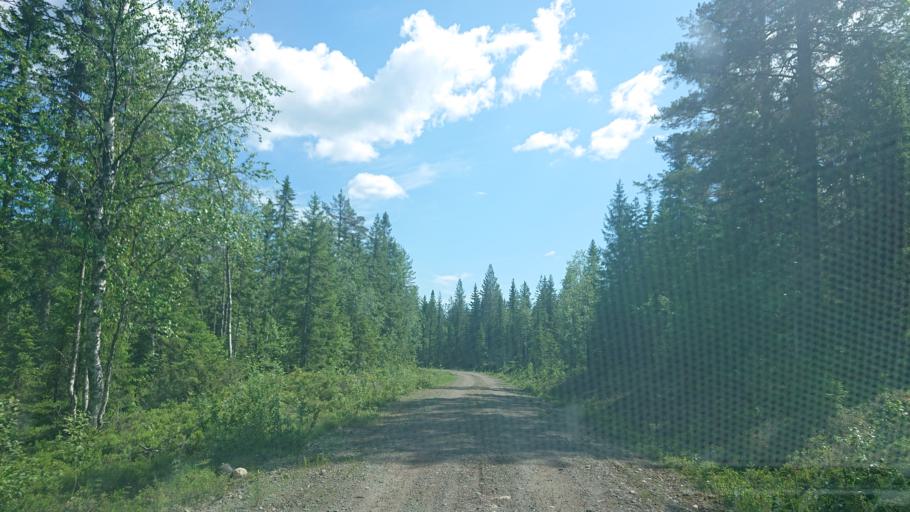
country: SE
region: Vaesternorrland
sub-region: Solleftea Kommun
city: Solleftea
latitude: 62.9336
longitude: 17.0827
